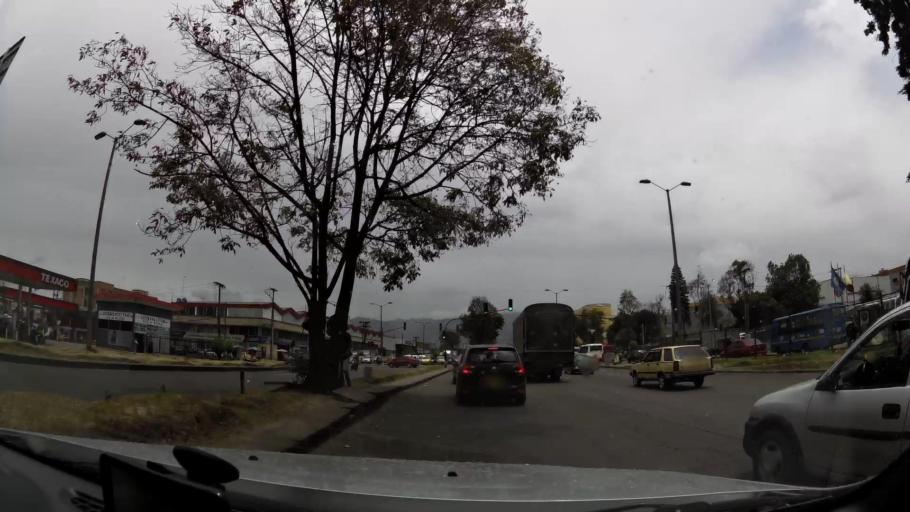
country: CO
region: Bogota D.C.
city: Bogota
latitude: 4.6348
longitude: -74.1153
